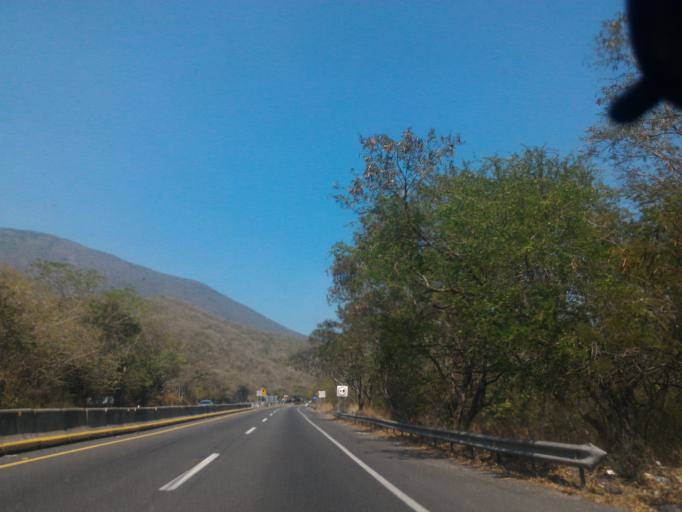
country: MX
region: Colima
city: Ixtlahuacan
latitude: 19.0286
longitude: -103.7945
